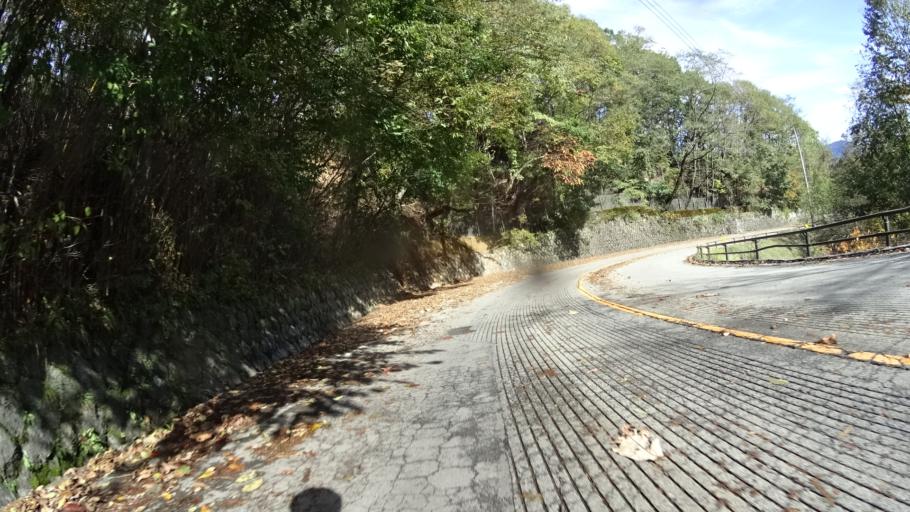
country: JP
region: Yamanashi
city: Enzan
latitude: 35.7877
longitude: 138.7992
